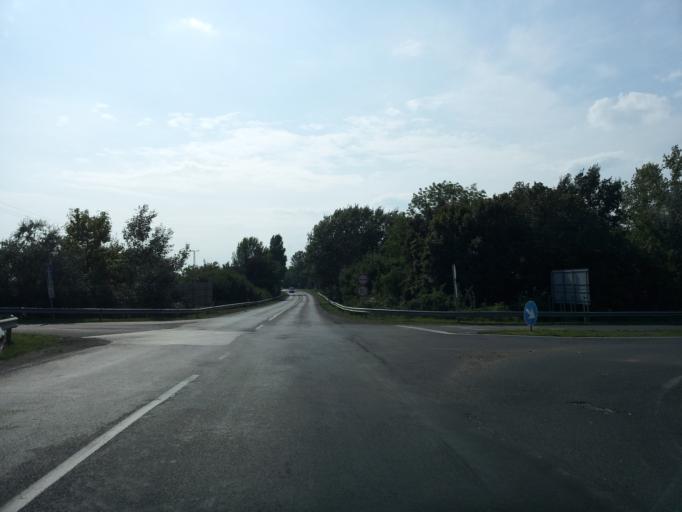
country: HU
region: Somogy
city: Balatonszabadi
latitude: 46.9304
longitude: 18.1359
